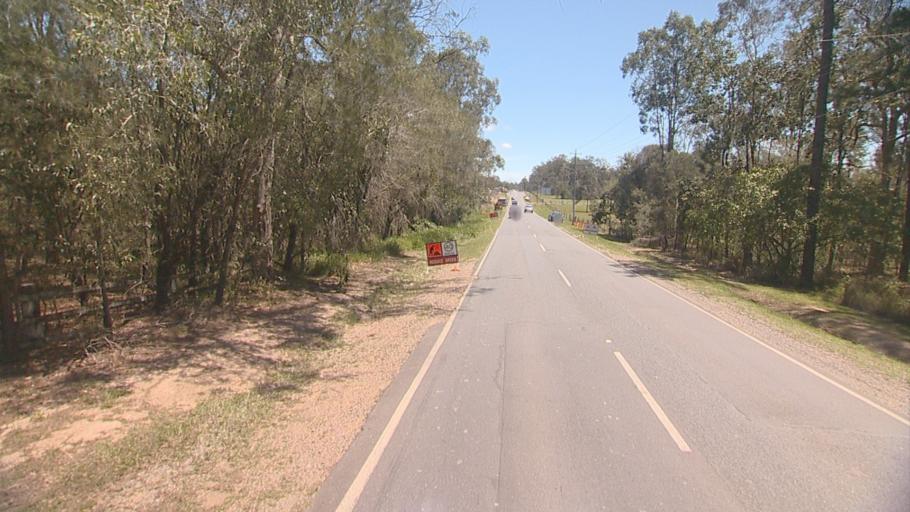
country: AU
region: Queensland
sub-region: Logan
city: Logan Reserve
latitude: -27.7077
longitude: 153.0863
